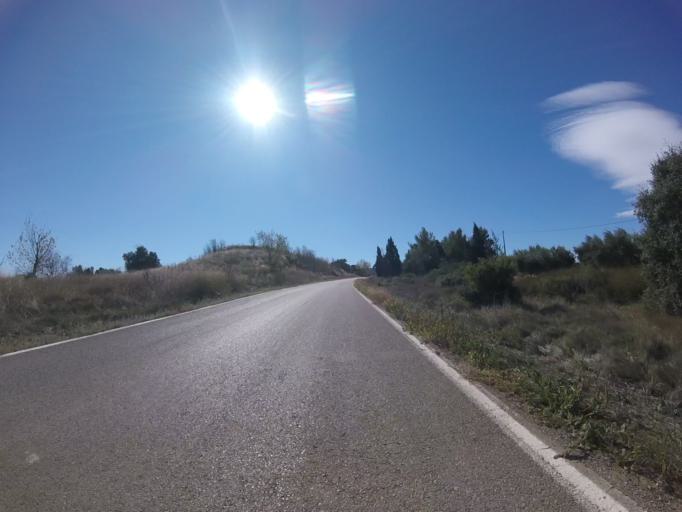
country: ES
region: Valencia
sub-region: Provincia de Castello
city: Albocasser
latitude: 40.3684
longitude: 0.0202
